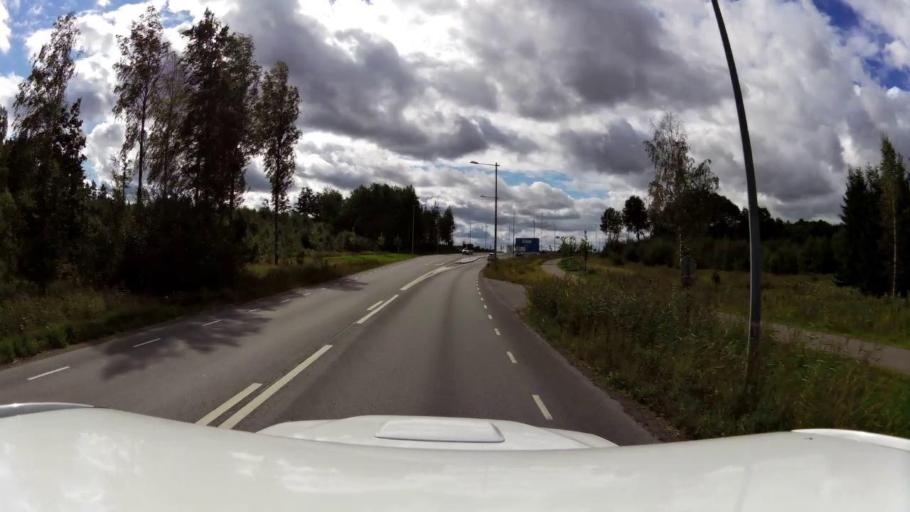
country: SE
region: OEstergoetland
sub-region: Linkopings Kommun
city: Linkoping
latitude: 58.3892
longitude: 15.5938
